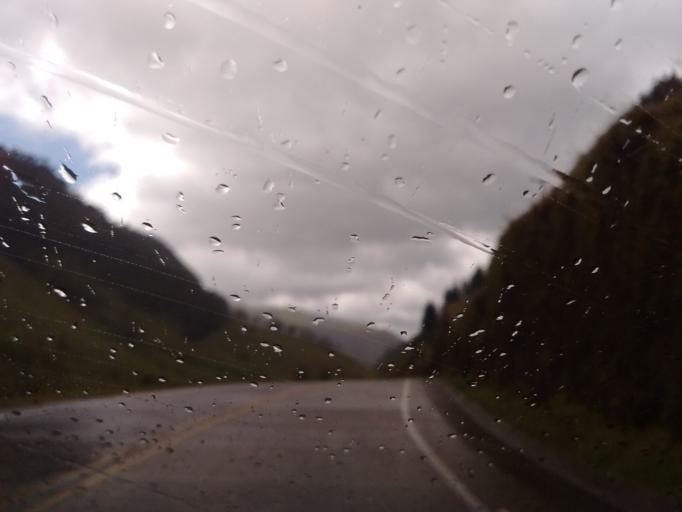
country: CO
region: Cauca
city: Paispamba
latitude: 2.2910
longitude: -76.5125
